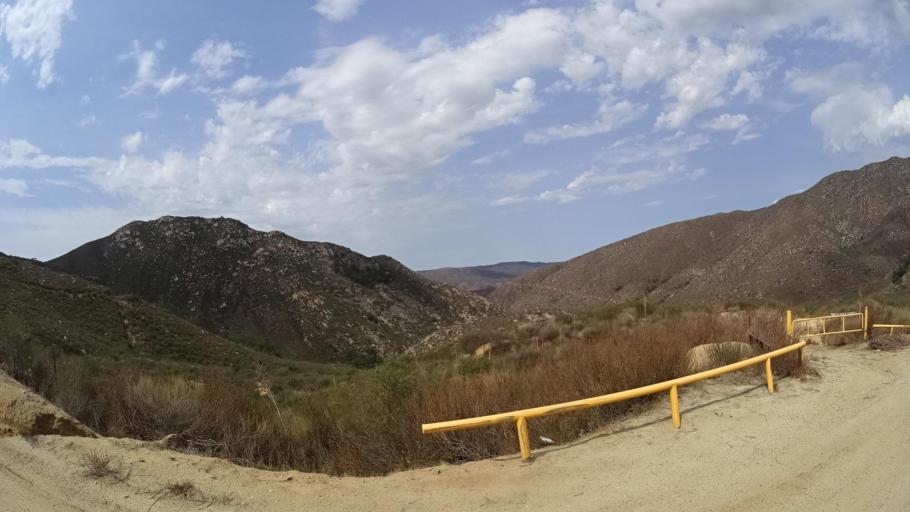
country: US
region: California
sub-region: San Diego County
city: Ramona
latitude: 33.1192
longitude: -116.8113
